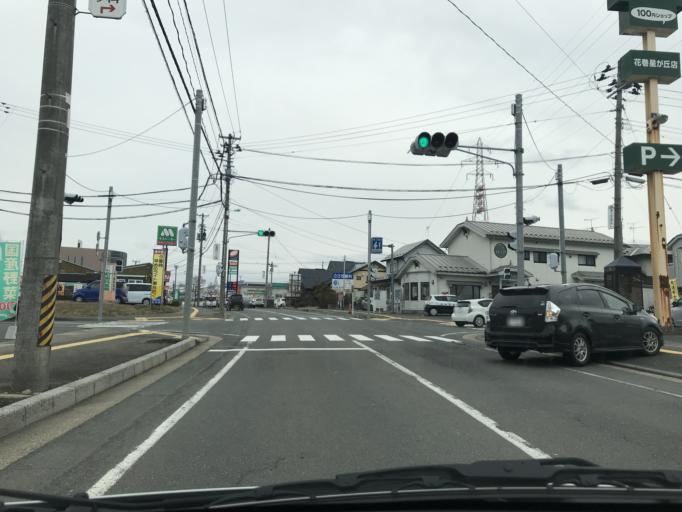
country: JP
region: Iwate
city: Hanamaki
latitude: 39.4017
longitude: 141.1055
